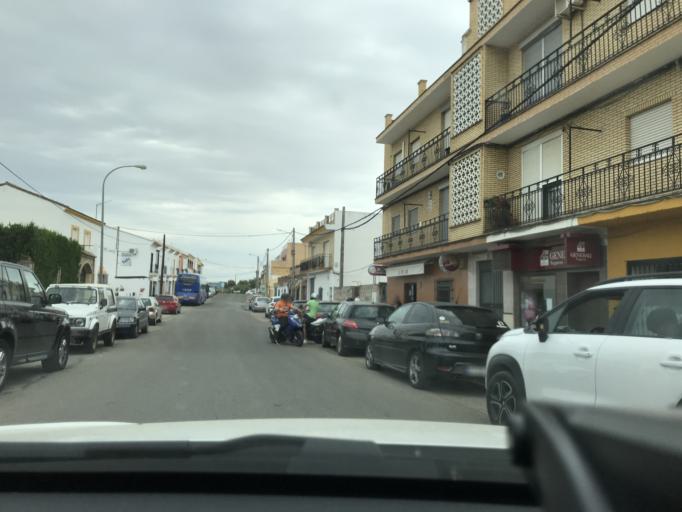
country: ES
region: Andalusia
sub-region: Provincia de Sevilla
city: Villanueva del Rio y Minas
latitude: 37.6484
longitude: -5.7114
